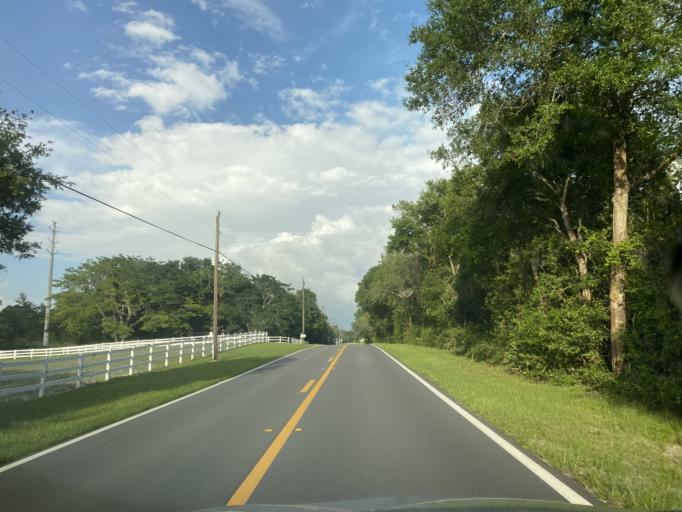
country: US
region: Florida
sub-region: Seminole County
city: Midway
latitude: 28.8453
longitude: -81.1669
